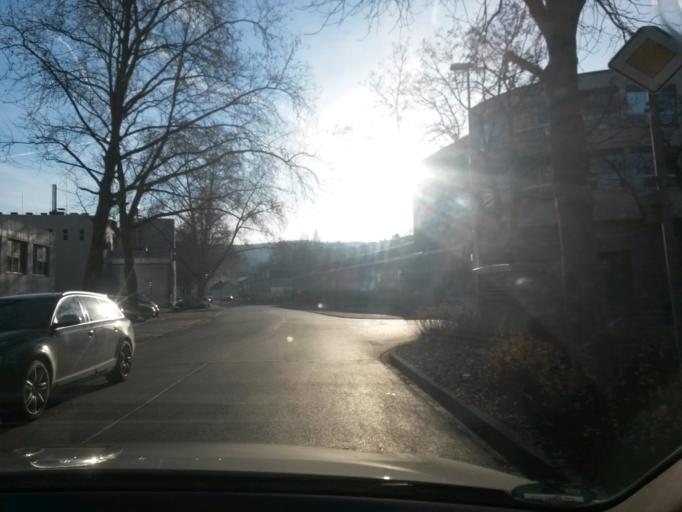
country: DE
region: Baden-Wuerttemberg
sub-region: Karlsruhe Region
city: Birkenfeld
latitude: 48.8757
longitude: 8.6462
